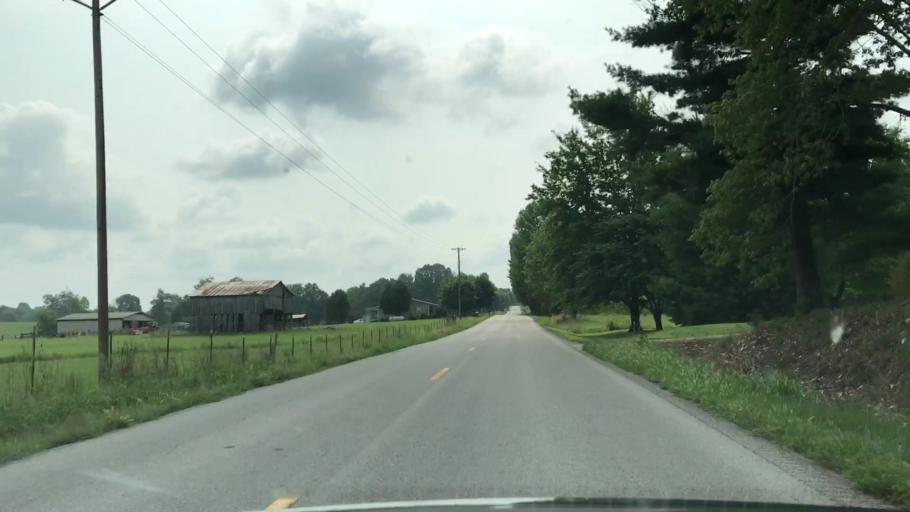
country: US
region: Kentucky
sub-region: Edmonson County
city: Brownsville
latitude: 37.1280
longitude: -86.1618
